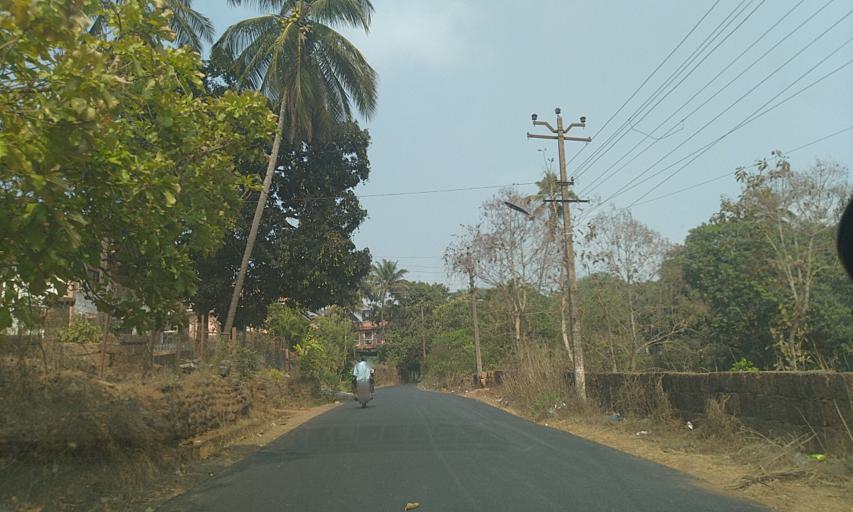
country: IN
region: Goa
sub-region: South Goa
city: Raia
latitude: 15.3080
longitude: 73.9764
